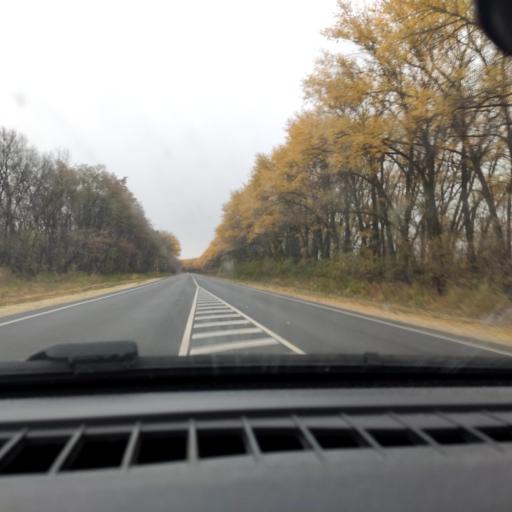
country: RU
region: Voronezj
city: Uryv-Pokrovka
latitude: 51.1820
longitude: 39.0825
